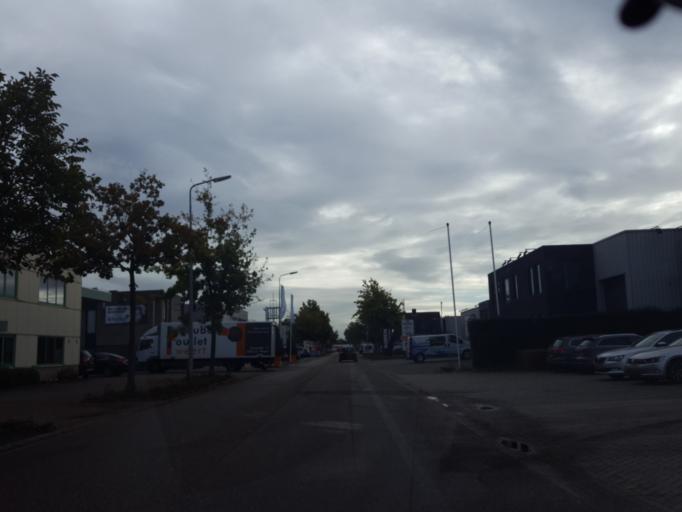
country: NL
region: Limburg
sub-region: Gemeente Weert
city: Weert
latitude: 51.2476
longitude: 5.7327
